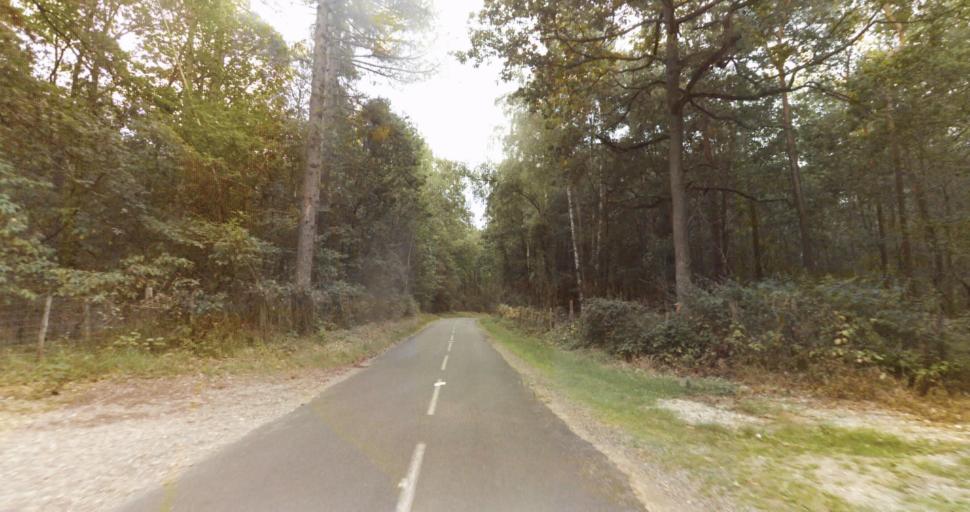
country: FR
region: Haute-Normandie
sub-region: Departement de l'Eure
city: Croth
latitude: 48.8562
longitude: 1.3617
